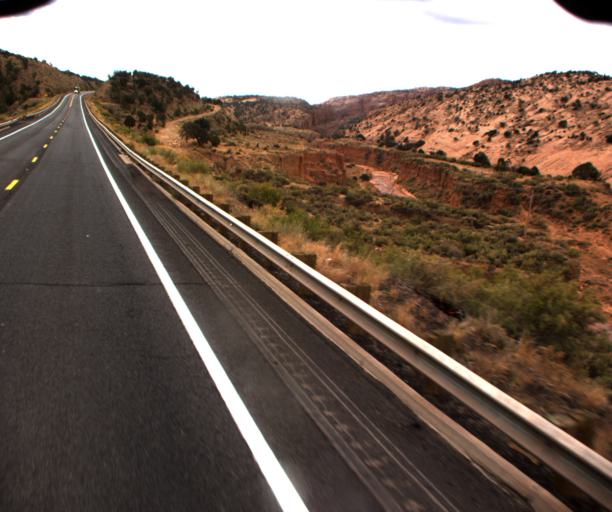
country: US
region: Arizona
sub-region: Navajo County
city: Kayenta
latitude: 36.6565
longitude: -110.4228
